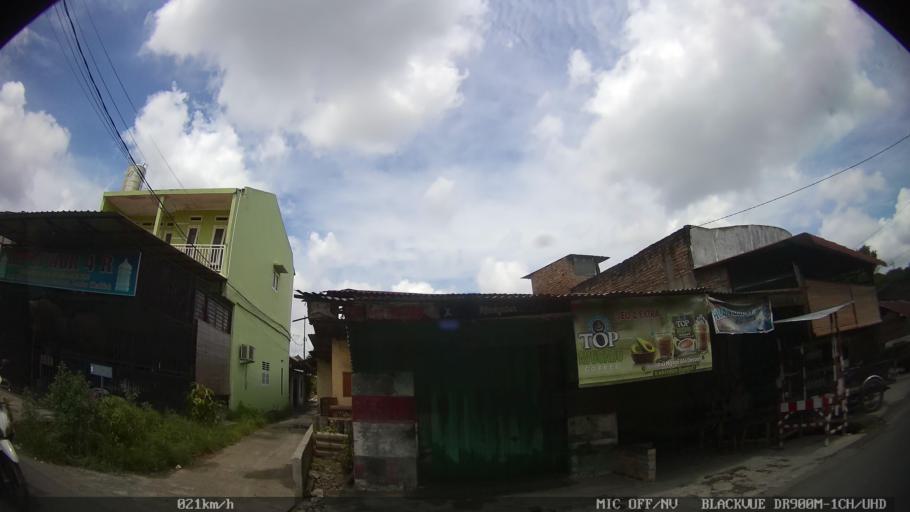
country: ID
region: North Sumatra
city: Medan
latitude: 3.6055
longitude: 98.7471
